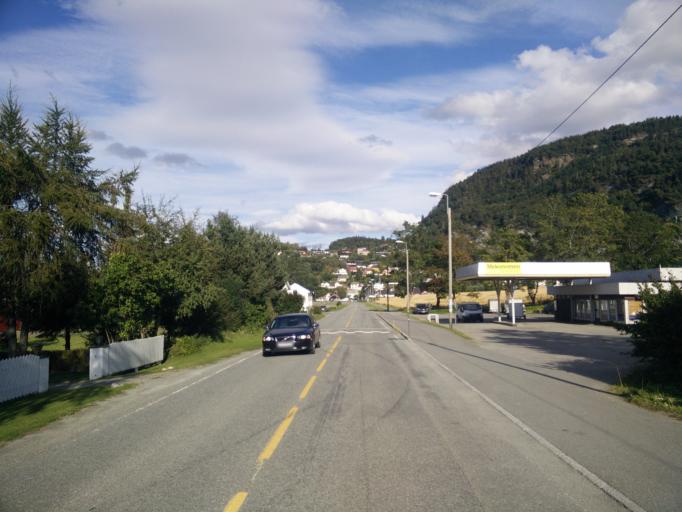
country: NO
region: Sor-Trondelag
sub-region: Melhus
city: Melhus
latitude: 63.3132
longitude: 10.1861
